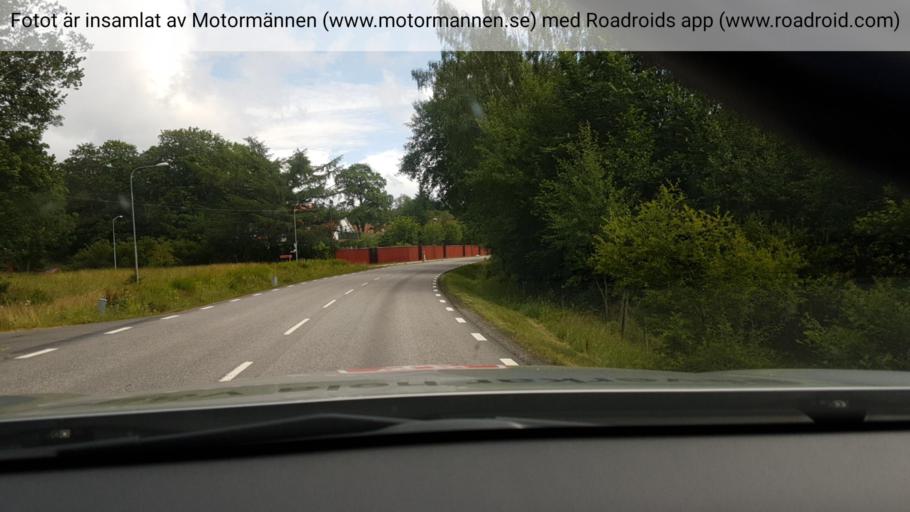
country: SE
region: Vaestra Goetaland
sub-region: Tranemo Kommun
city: Tranemo
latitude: 57.4740
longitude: 13.2608
